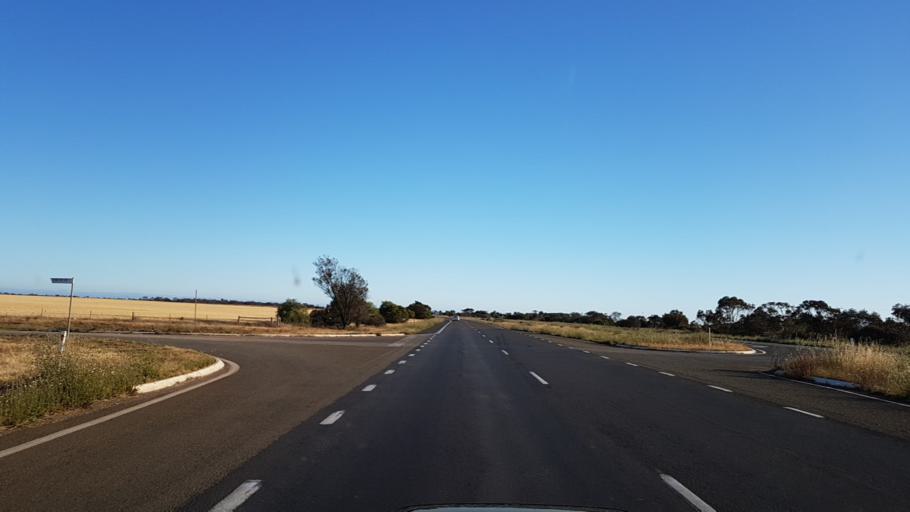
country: AU
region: South Australia
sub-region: Mallala
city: Mallala
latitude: -34.4216
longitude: 138.3342
